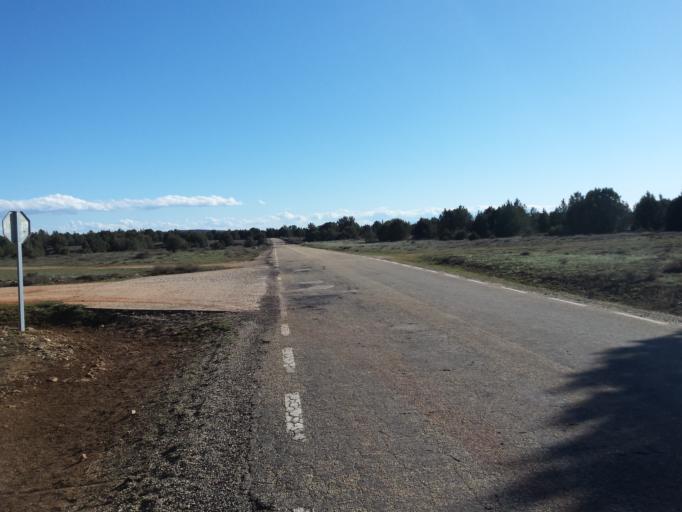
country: ES
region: Castille and Leon
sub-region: Provincia de Soria
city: Calatanazor
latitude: 41.7444
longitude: -2.7757
